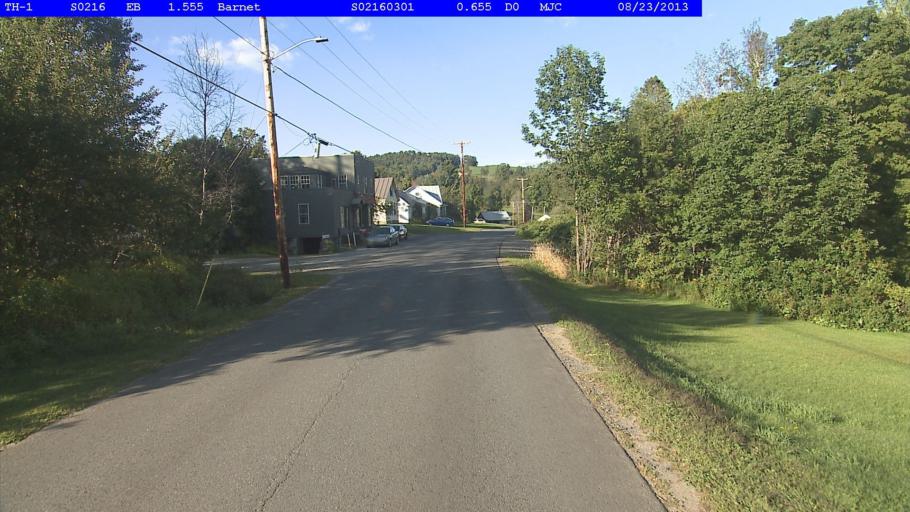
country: US
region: Vermont
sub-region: Caledonia County
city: Saint Johnsbury
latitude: 44.3092
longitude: -72.1390
